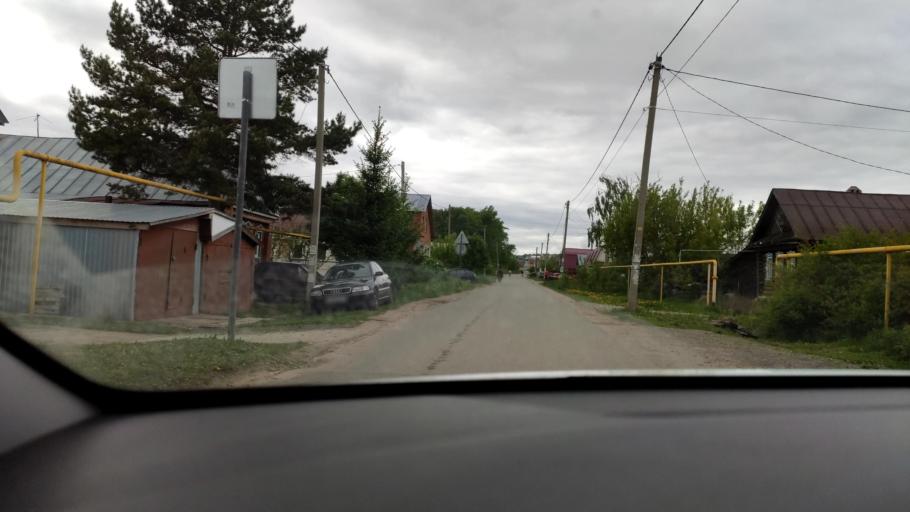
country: RU
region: Tatarstan
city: Stolbishchi
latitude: 55.7489
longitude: 49.3007
